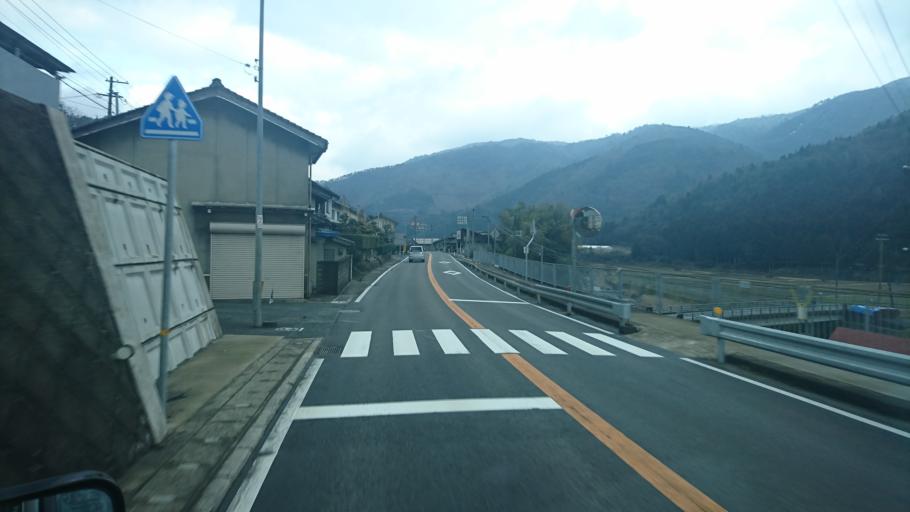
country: JP
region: Hyogo
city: Toyooka
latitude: 35.3813
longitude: 134.6591
